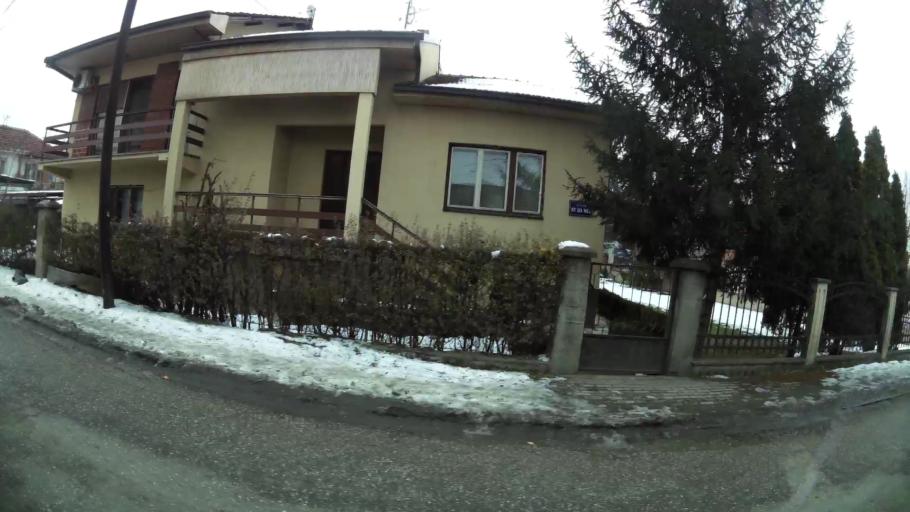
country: MK
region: Butel
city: Butel
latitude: 42.0357
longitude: 21.4490
